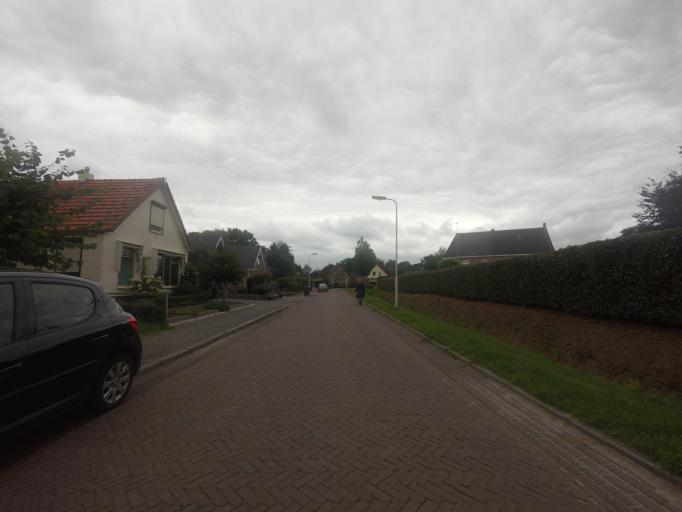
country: NL
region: Friesland
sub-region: Gemeente Weststellingwerf
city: Noordwolde
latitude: 52.9106
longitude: 6.2007
